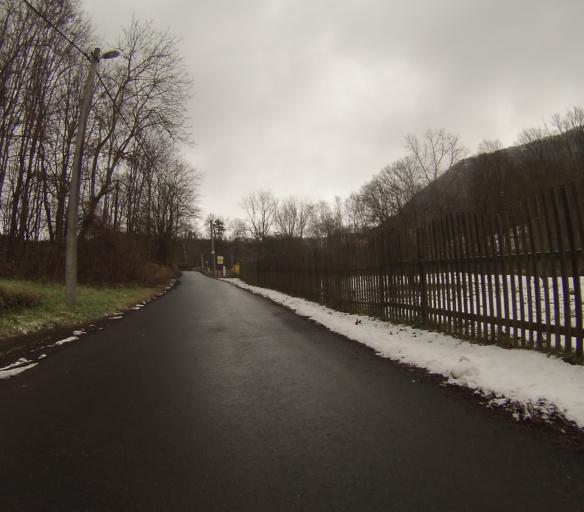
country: CZ
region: Ustecky
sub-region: Okres Decin
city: Decin
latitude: 50.7575
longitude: 14.2591
